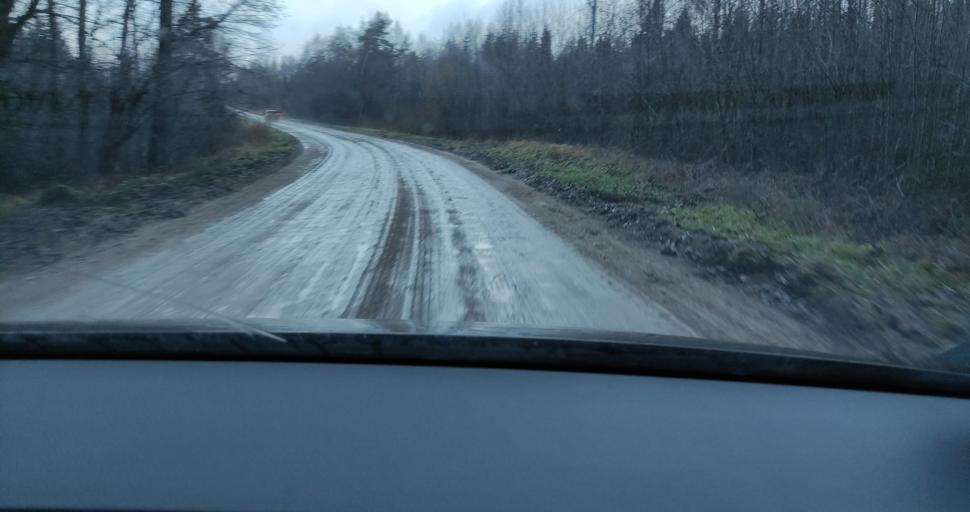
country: LV
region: Skrunda
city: Skrunda
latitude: 56.7069
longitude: 22.2088
